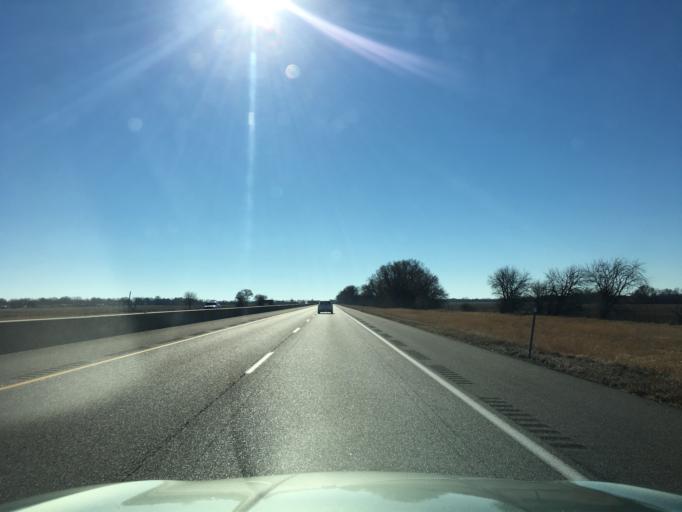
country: US
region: Kansas
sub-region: Sumner County
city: Belle Plaine
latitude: 37.4483
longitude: -97.3222
